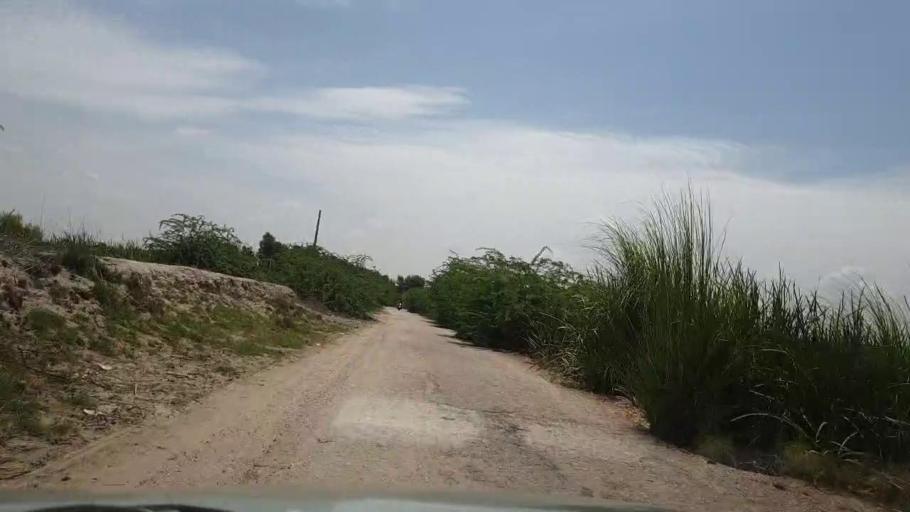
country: PK
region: Sindh
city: Bozdar
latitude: 27.0773
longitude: 68.9681
